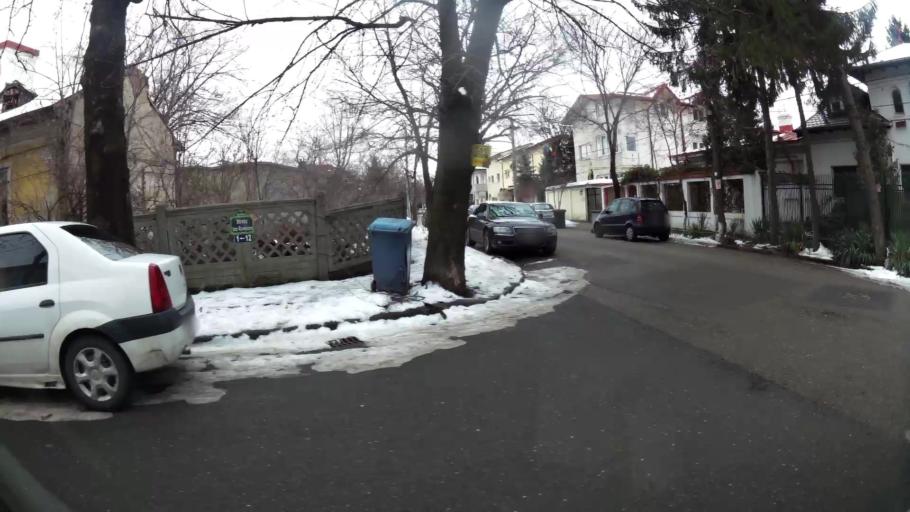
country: RO
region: Bucuresti
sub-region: Municipiul Bucuresti
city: Bucuresti
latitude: 44.4222
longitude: 26.0556
